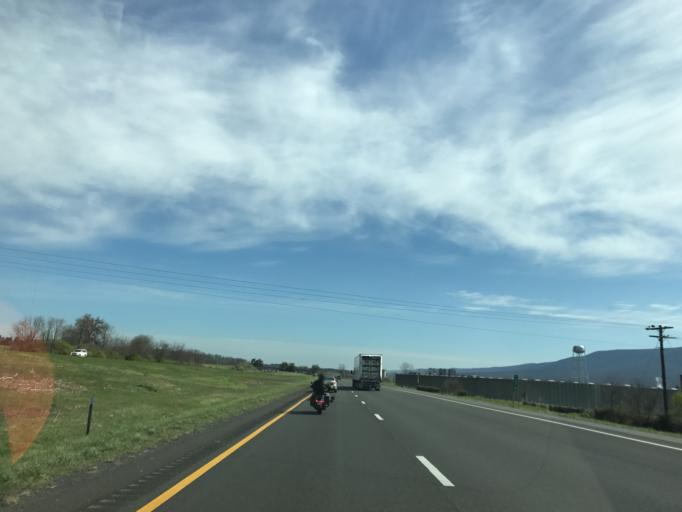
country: US
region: Virginia
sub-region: Shenandoah County
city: Mount Jackson
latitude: 38.7662
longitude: -78.6283
